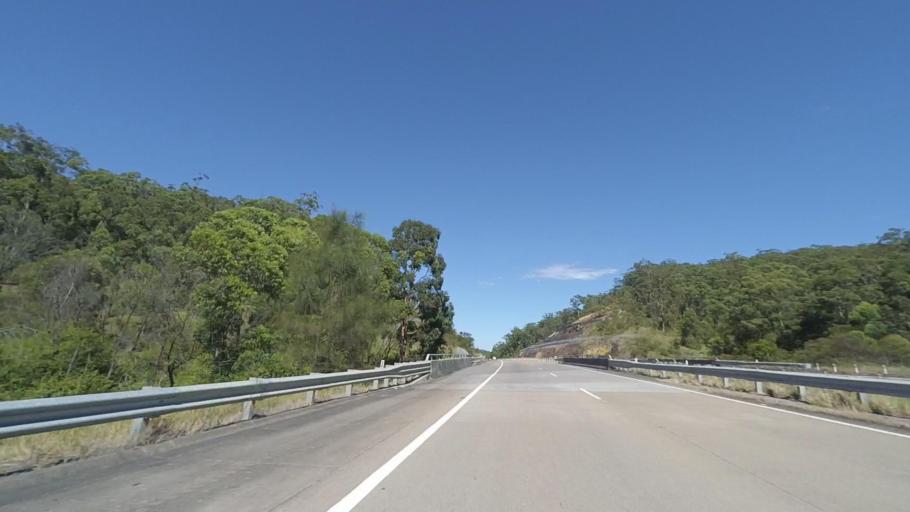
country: AU
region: New South Wales
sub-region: Port Stephens Shire
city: Port Stephens
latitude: -32.6208
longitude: 151.9717
